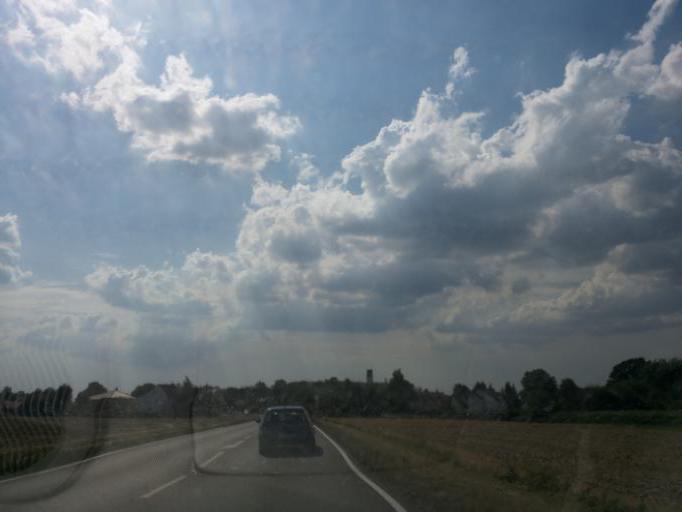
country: DE
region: Bavaria
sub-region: Upper Bavaria
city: Lenting
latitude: 48.7957
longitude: 11.4480
